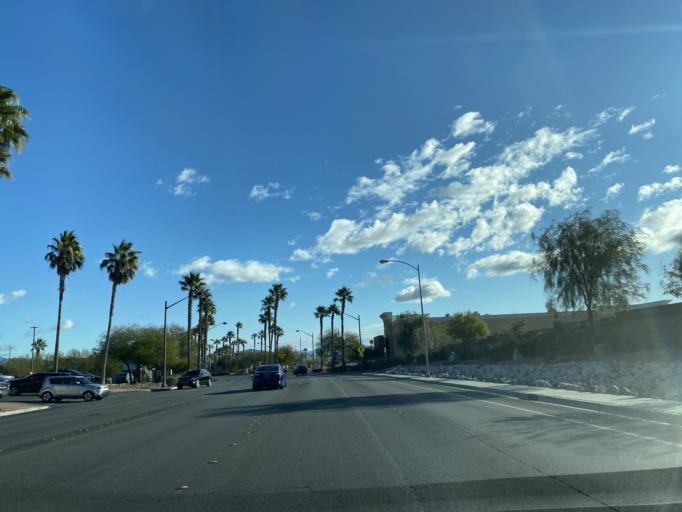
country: US
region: Nevada
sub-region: Clark County
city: Las Vegas
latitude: 36.2702
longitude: -115.2707
